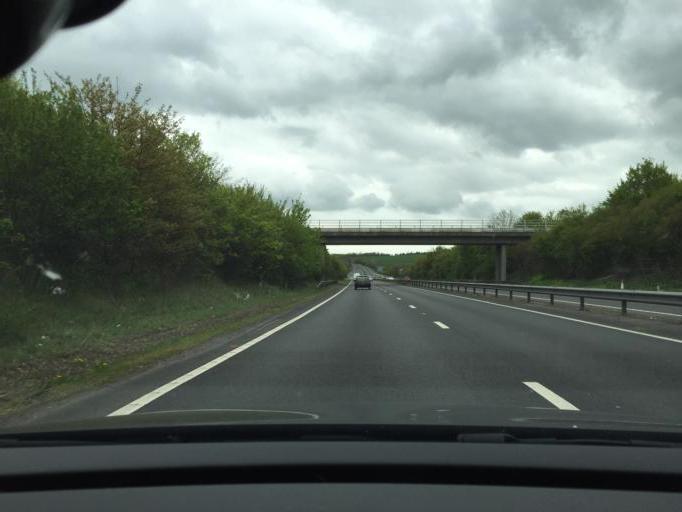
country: GB
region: England
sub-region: Oxfordshire
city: Harwell
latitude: 51.5588
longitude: -1.3008
